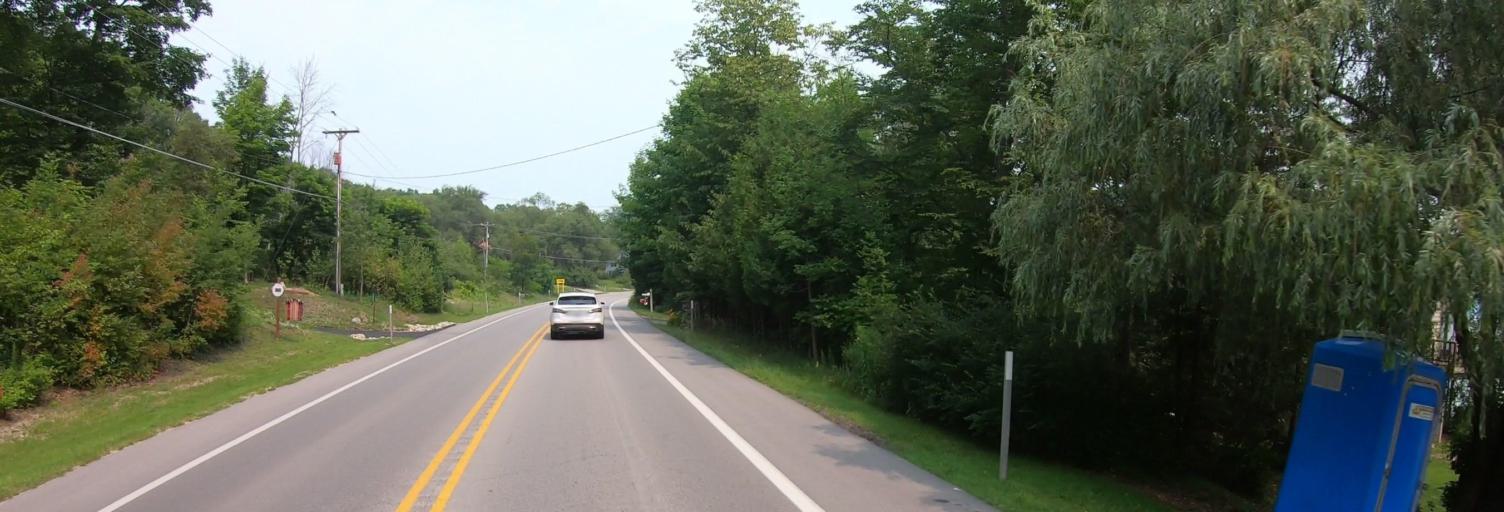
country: US
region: Michigan
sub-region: Leelanau County
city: Leland
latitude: 45.0008
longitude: -85.7717
